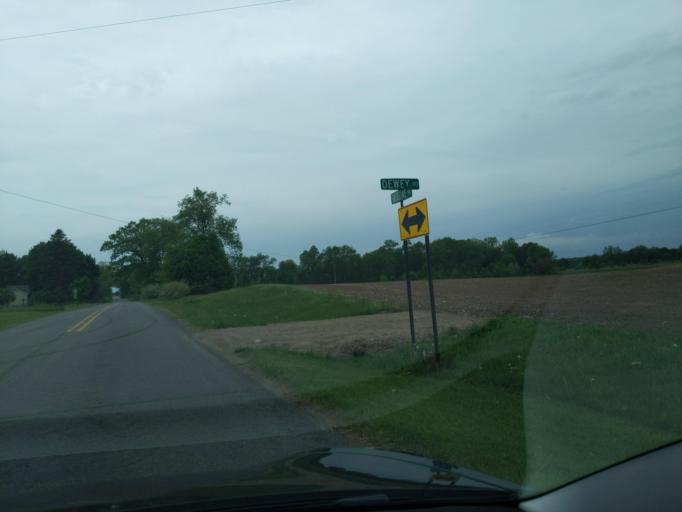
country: US
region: Michigan
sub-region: Ingham County
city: Stockbridge
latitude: 42.4268
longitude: -84.2250
